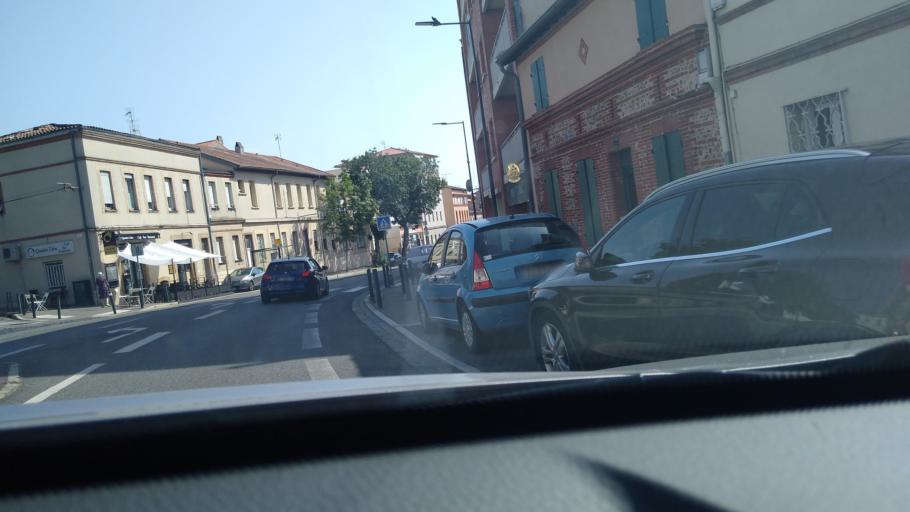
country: FR
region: Midi-Pyrenees
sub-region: Departement de la Haute-Garonne
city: Toulouse
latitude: 43.6238
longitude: 1.4589
